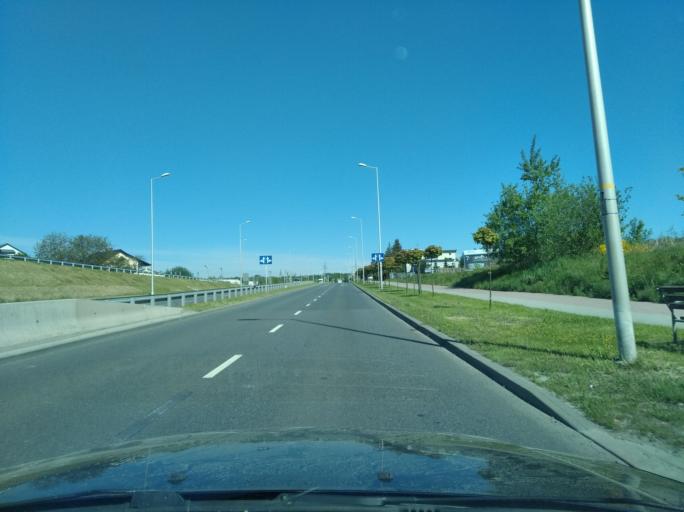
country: PL
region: Subcarpathian Voivodeship
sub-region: Powiat rzeszowski
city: Boguchwala
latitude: 50.0111
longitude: 21.9640
